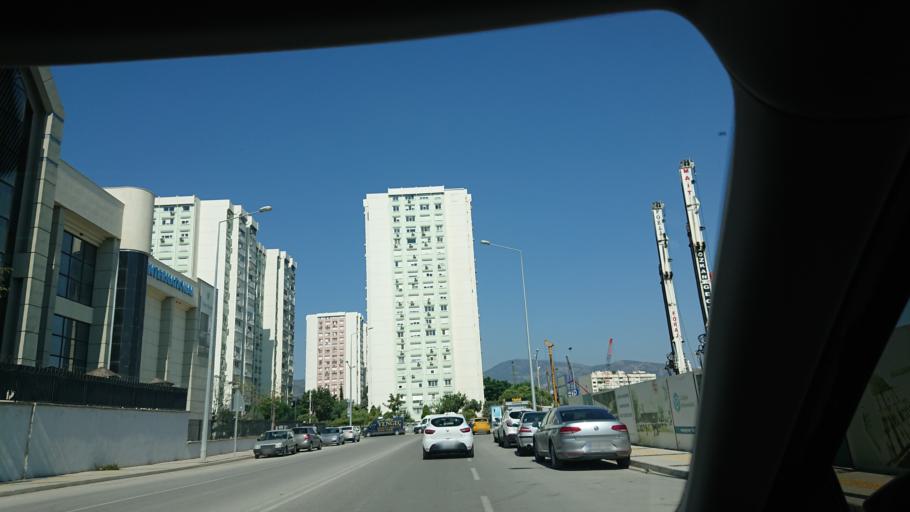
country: TR
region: Izmir
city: Karsiyaka
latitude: 38.4676
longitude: 27.0805
